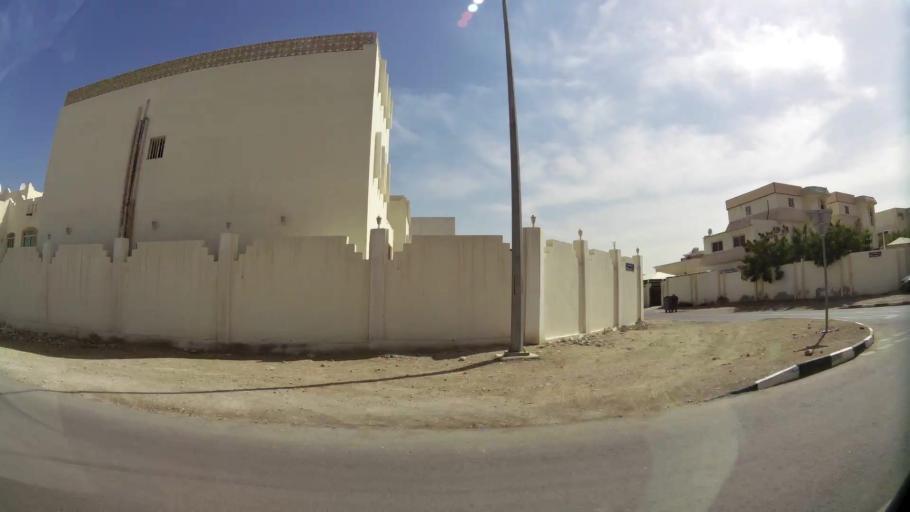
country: QA
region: Baladiyat ar Rayyan
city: Ar Rayyan
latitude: 25.2765
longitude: 51.4212
